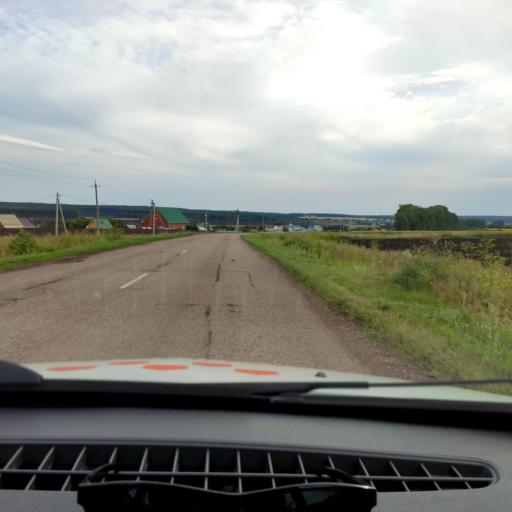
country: RU
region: Bashkortostan
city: Avdon
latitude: 54.5002
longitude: 55.6182
